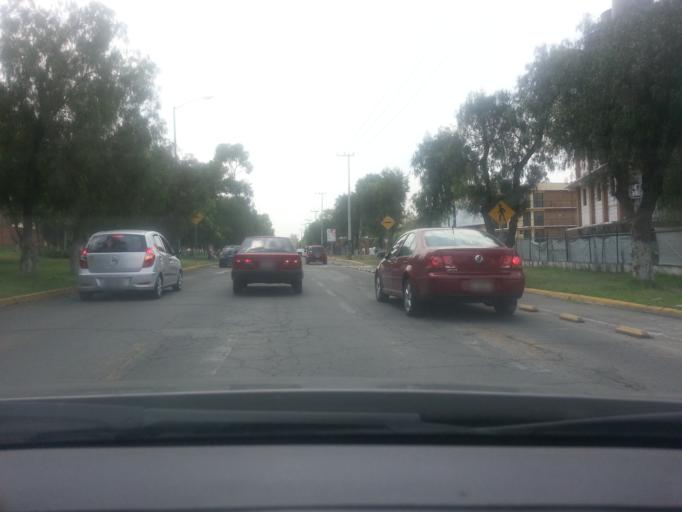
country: MX
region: Mexico
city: Cuautitlan Izcalli
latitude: 19.6534
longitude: -99.2164
